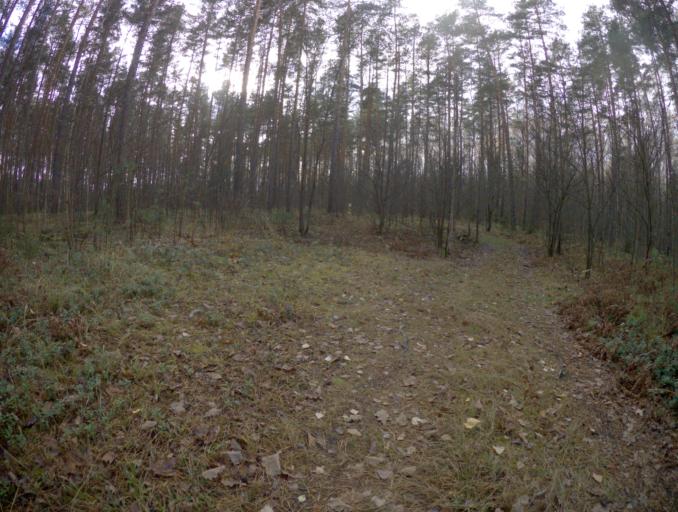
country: RU
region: Vladimir
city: Raduzhnyy
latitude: 56.0562
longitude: 40.3213
